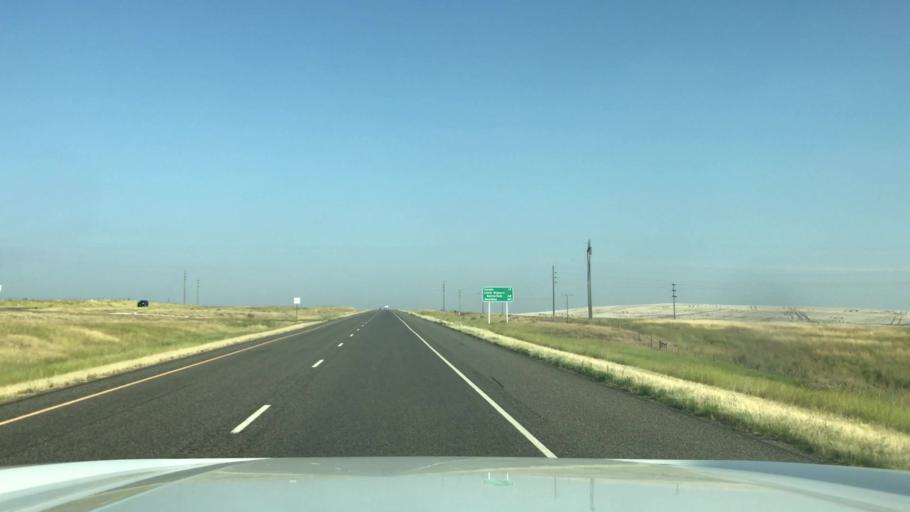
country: US
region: Montana
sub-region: Big Horn County
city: Hardin
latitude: 45.7740
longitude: -107.9406
